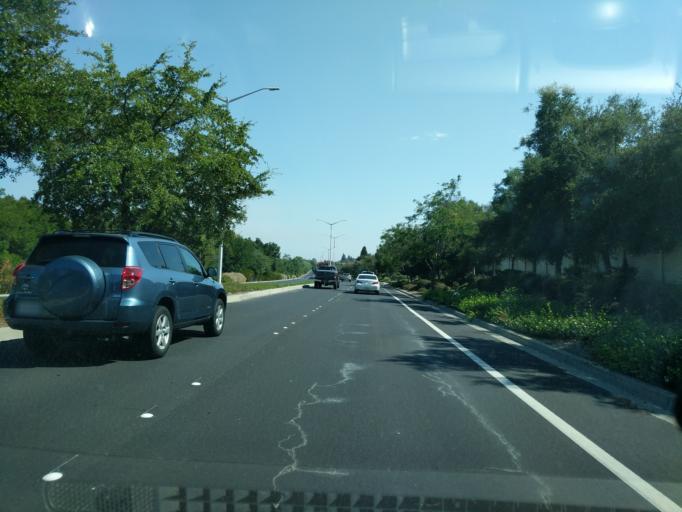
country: US
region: California
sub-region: Contra Costa County
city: San Ramon
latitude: 37.7446
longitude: -121.9566
